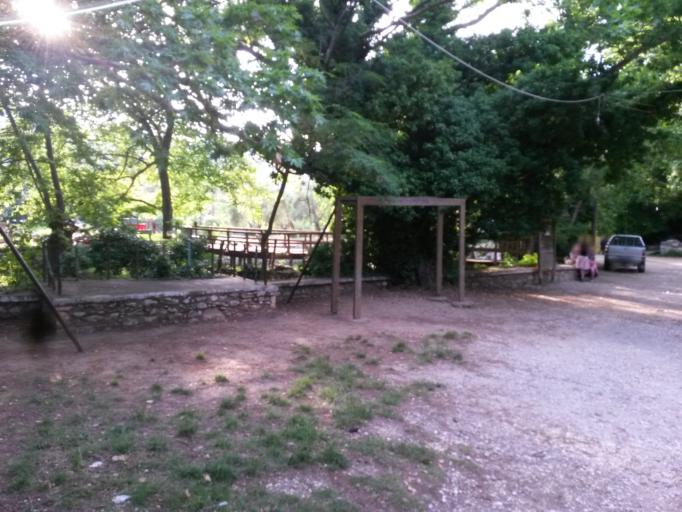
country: GR
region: North Aegean
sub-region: Nomos Lesvou
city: Agiasos
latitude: 39.0960
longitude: 26.4021
